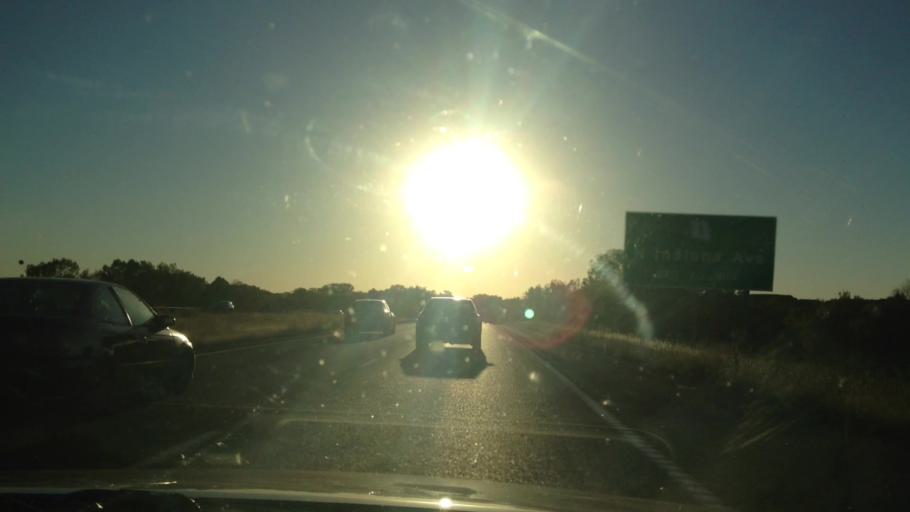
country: US
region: Missouri
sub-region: Clay County
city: Pleasant Valley
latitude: 39.2427
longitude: -94.5208
